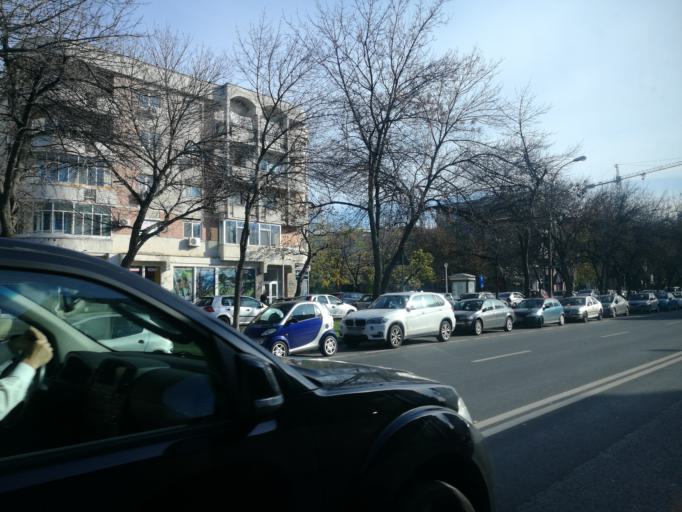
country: RO
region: Bucuresti
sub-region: Municipiul Bucuresti
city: Bucharest
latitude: 44.4812
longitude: 26.0923
